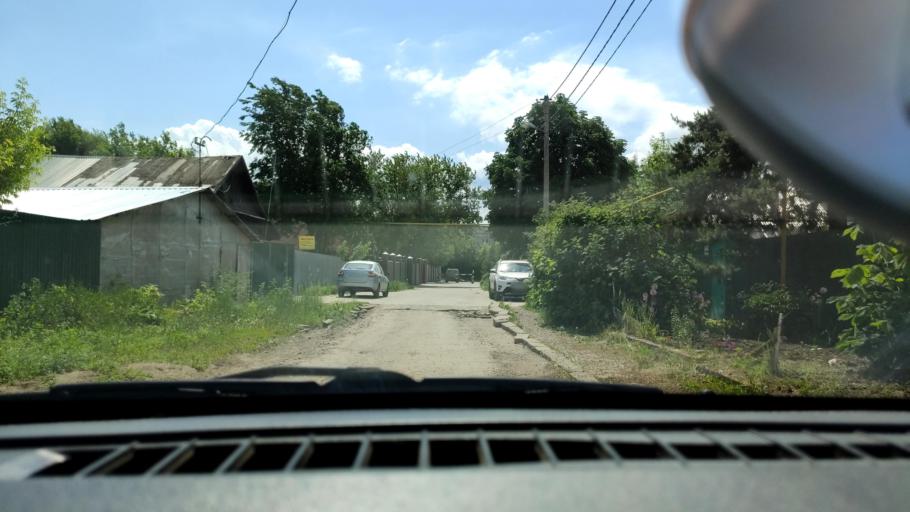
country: RU
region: Samara
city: Samara
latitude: 53.2128
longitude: 50.2602
